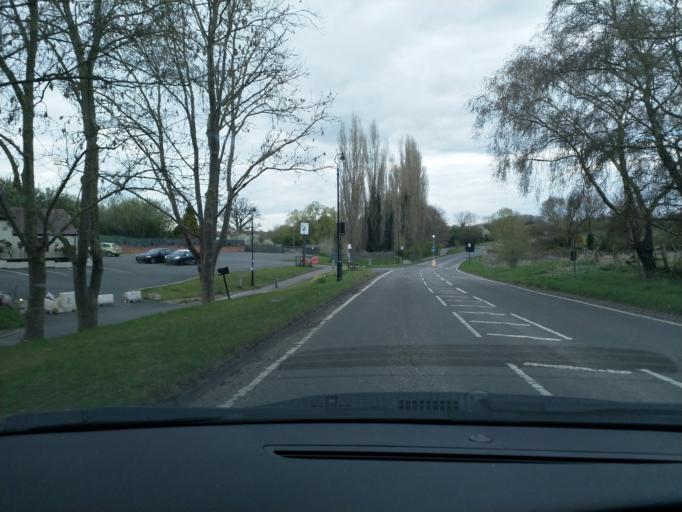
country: GB
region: England
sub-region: Warwickshire
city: Royal Leamington Spa
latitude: 52.2505
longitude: -1.5400
